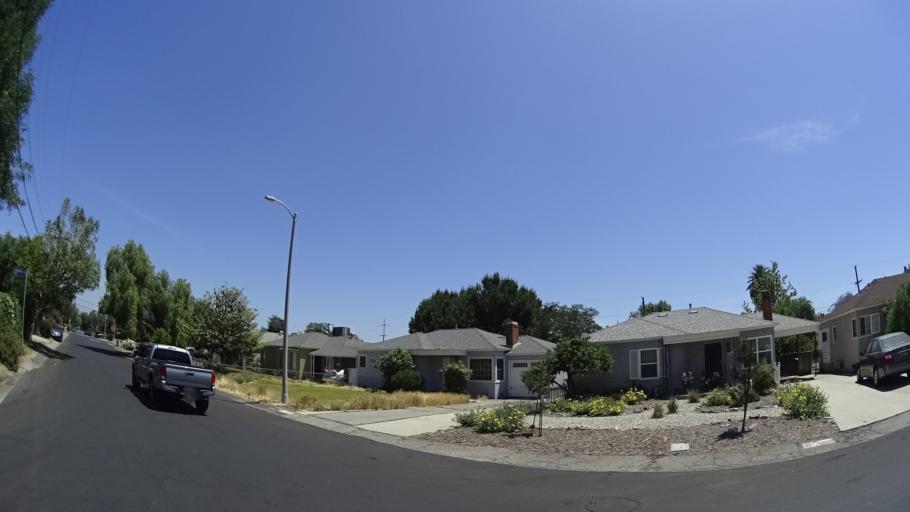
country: US
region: California
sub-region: Los Angeles County
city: North Hollywood
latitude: 34.1831
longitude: -118.3823
